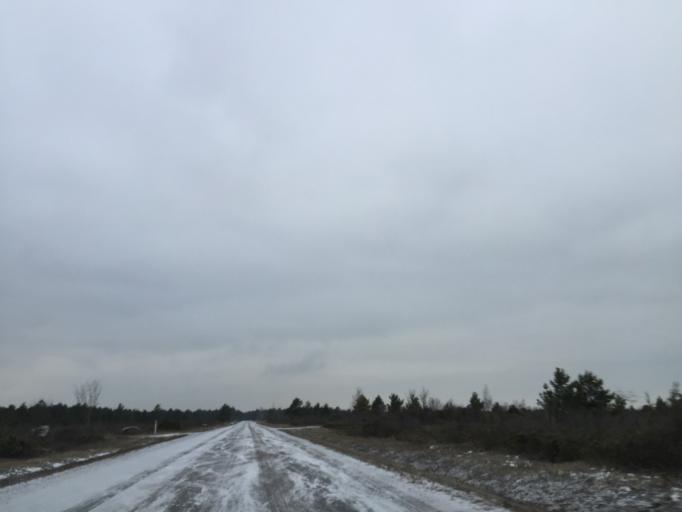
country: EE
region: Saare
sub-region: Orissaare vald
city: Orissaare
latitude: 58.6690
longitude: 23.2349
